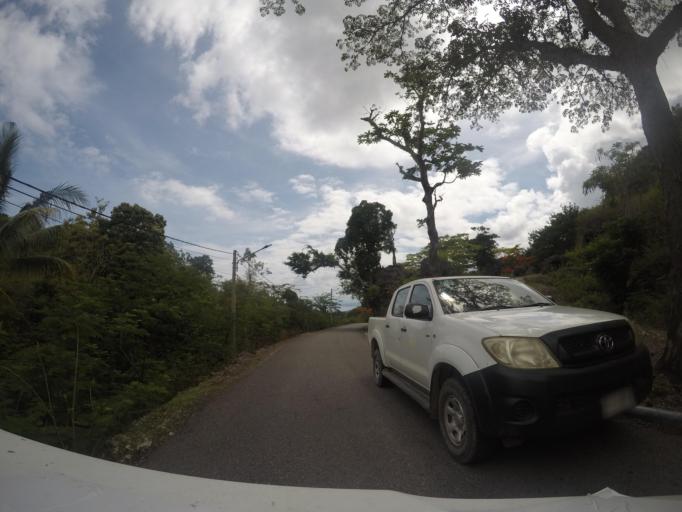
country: TL
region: Baucau
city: Baucau
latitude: -8.4629
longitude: 126.4354
